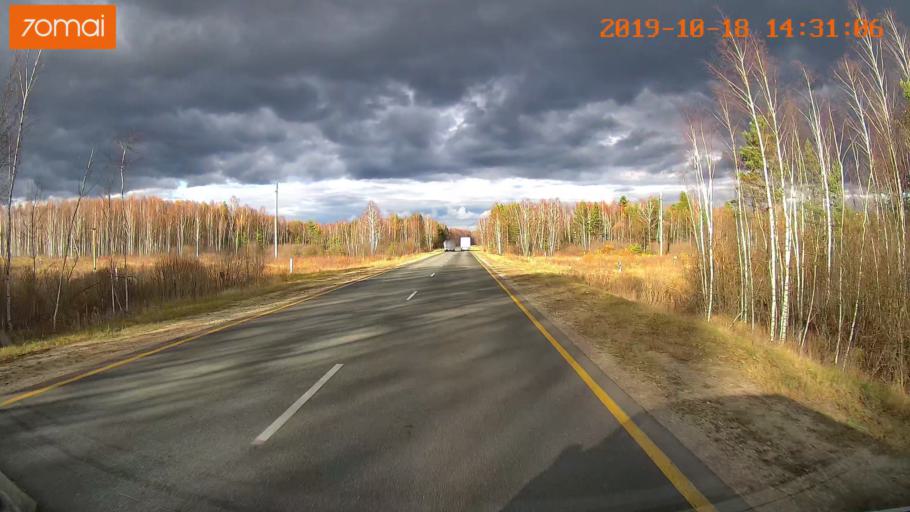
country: RU
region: Rjazan
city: Tuma
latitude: 55.1780
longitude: 40.5683
